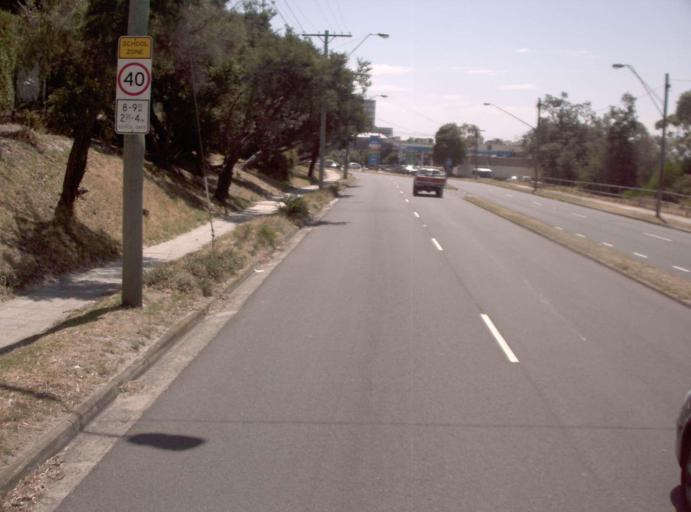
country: AU
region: Victoria
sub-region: Frankston
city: Frankston
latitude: -38.1485
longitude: 145.1264
